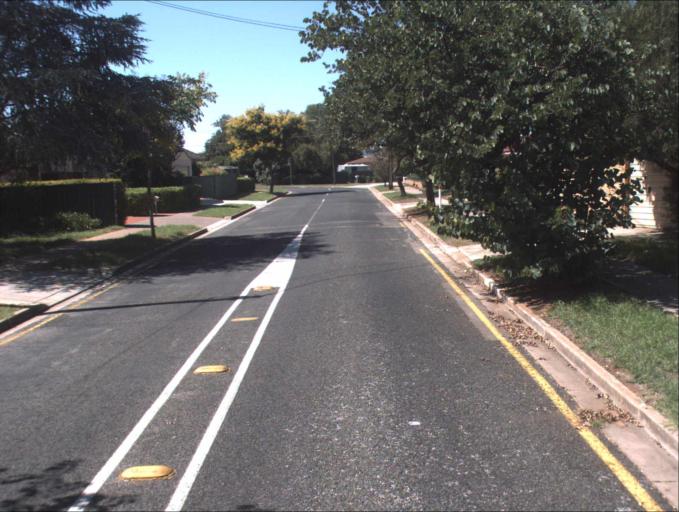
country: AU
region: South Australia
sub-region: Port Adelaide Enfield
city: Klemzig
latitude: -34.8849
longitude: 138.6352
